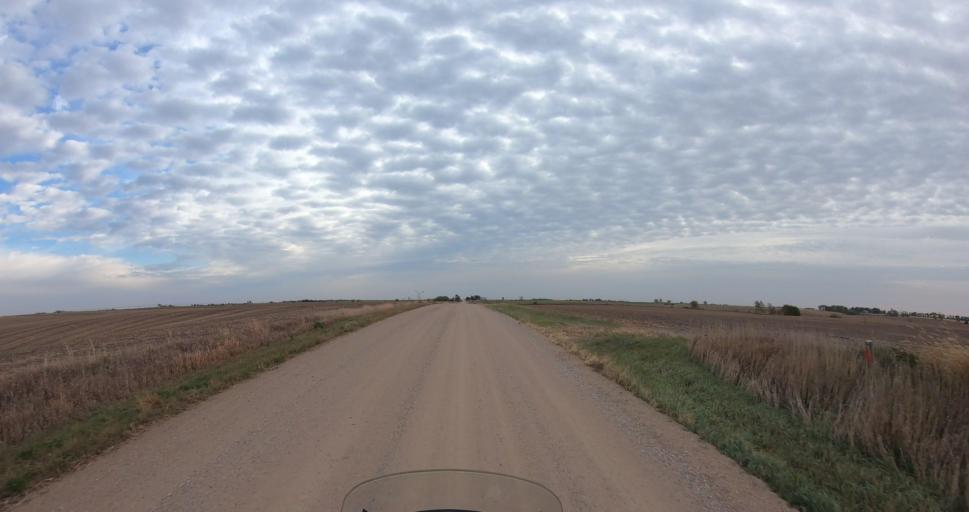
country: US
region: Nebraska
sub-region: Saline County
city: Friend
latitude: 40.8132
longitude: -97.3251
